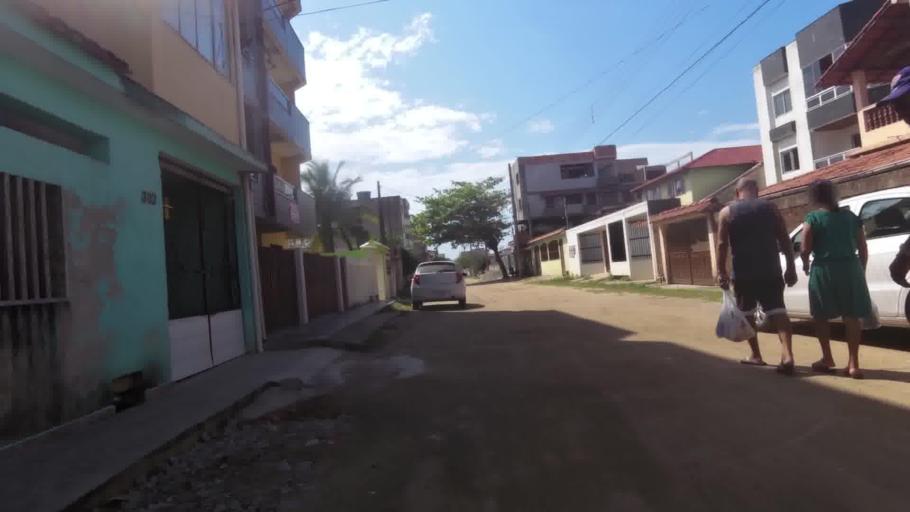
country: BR
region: Espirito Santo
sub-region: Piuma
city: Piuma
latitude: -20.8434
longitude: -40.7403
